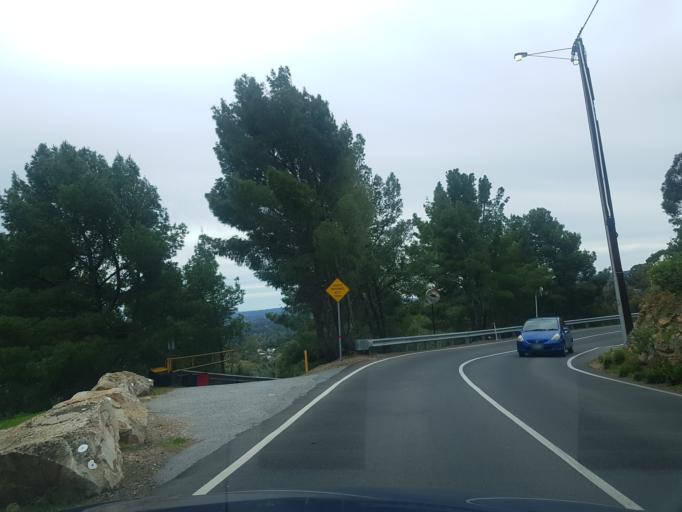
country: AU
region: South Australia
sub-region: Burnside
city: Mount Osmond
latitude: -34.9611
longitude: 138.6520
